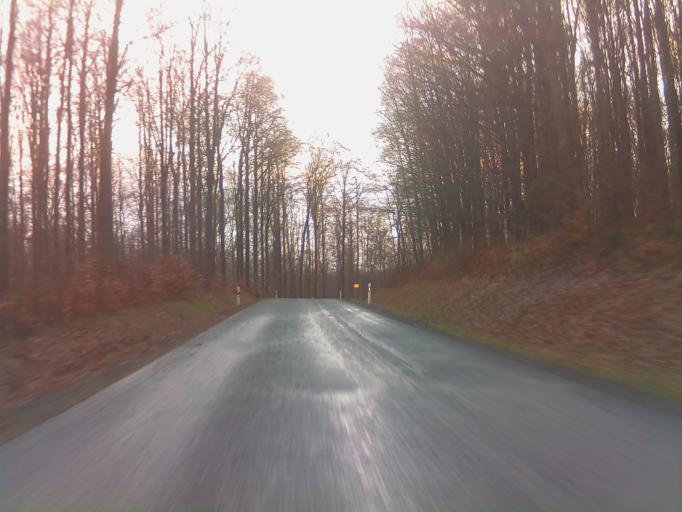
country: DE
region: Bavaria
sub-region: Regierungsbezirk Unterfranken
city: Hausen
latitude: 50.4850
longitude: 10.0927
